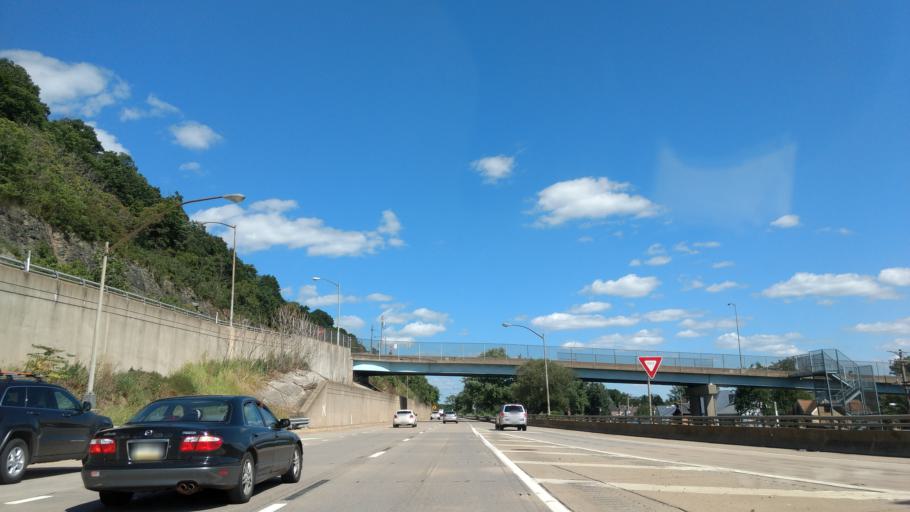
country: US
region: Pennsylvania
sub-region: Allegheny County
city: Emsworth
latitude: 40.5172
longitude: -80.1285
